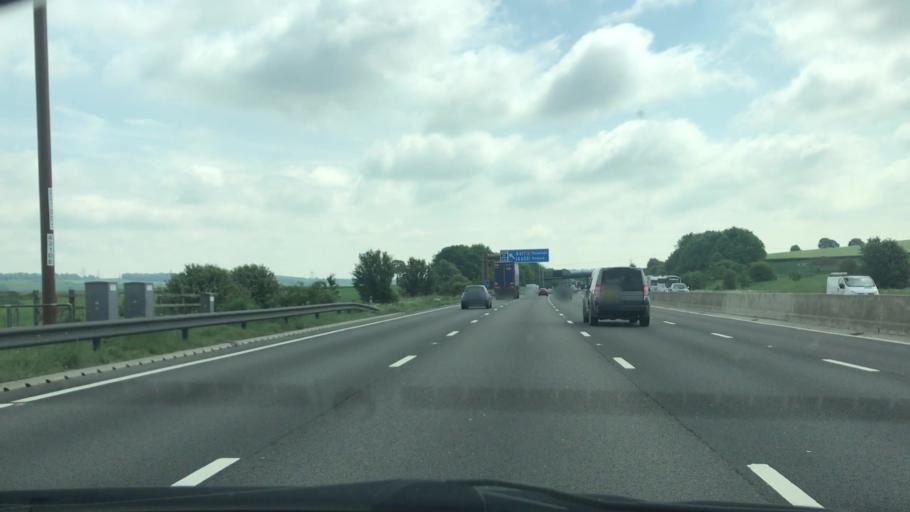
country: GB
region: England
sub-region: Derbyshire
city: Bolsover
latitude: 53.2196
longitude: -1.3273
